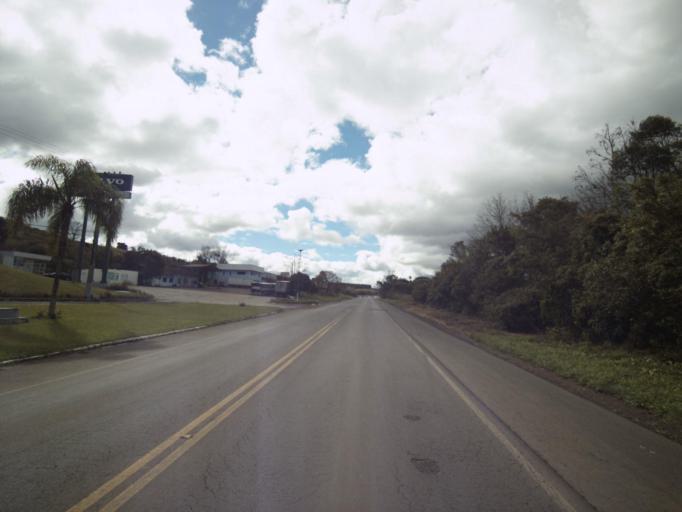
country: BR
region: Santa Catarina
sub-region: Concordia
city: Concordia
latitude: -27.2366
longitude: -51.9525
